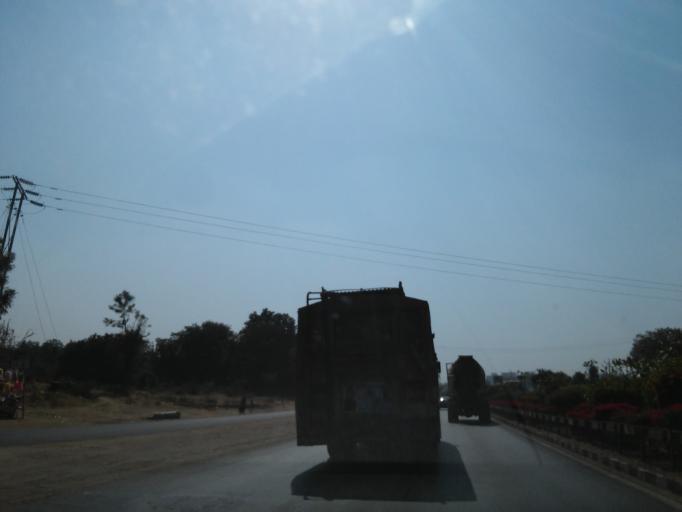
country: IN
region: Gujarat
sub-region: Gandhinagar
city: Adalaj
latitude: 23.1462
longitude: 72.5471
